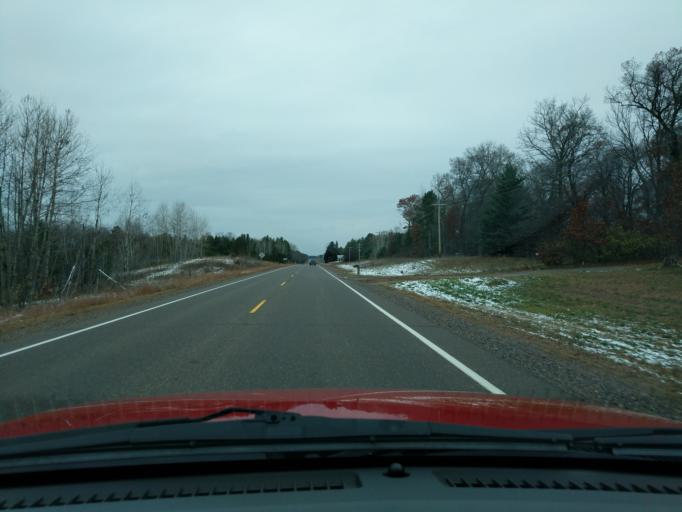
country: US
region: Wisconsin
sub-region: Burnett County
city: Siren
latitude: 45.8088
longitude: -92.1802
